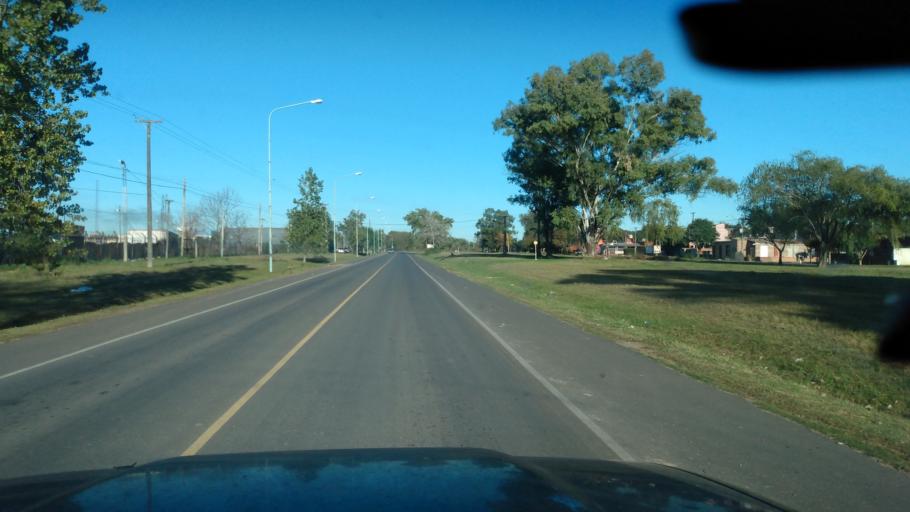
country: AR
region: Buenos Aires
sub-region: Partido de Lujan
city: Lujan
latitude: -34.5625
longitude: -59.1383
